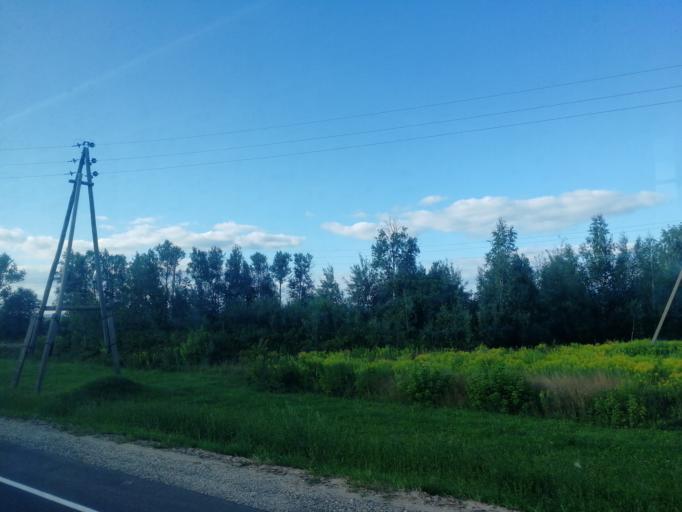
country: RU
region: Tula
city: Leninskiy
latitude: 54.2470
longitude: 37.3240
